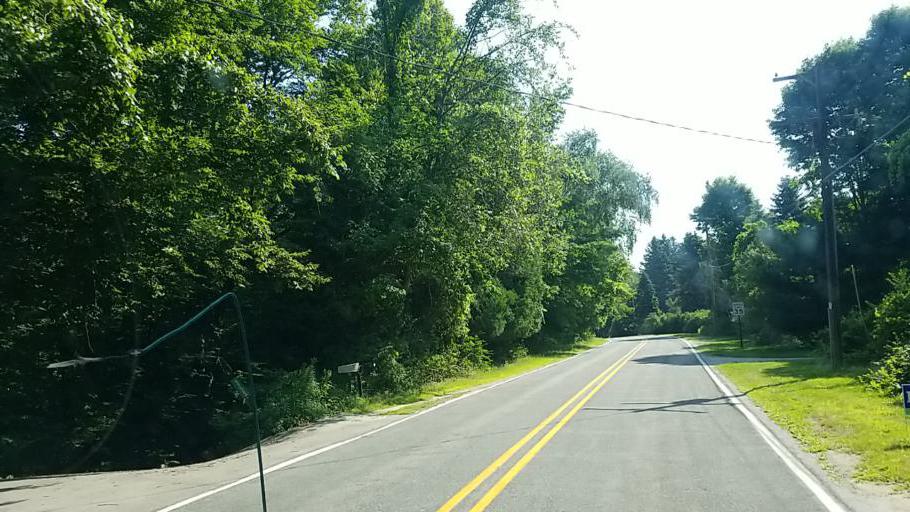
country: US
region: Michigan
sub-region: Muskegon County
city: Whitehall
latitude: 43.3691
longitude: -86.3860
